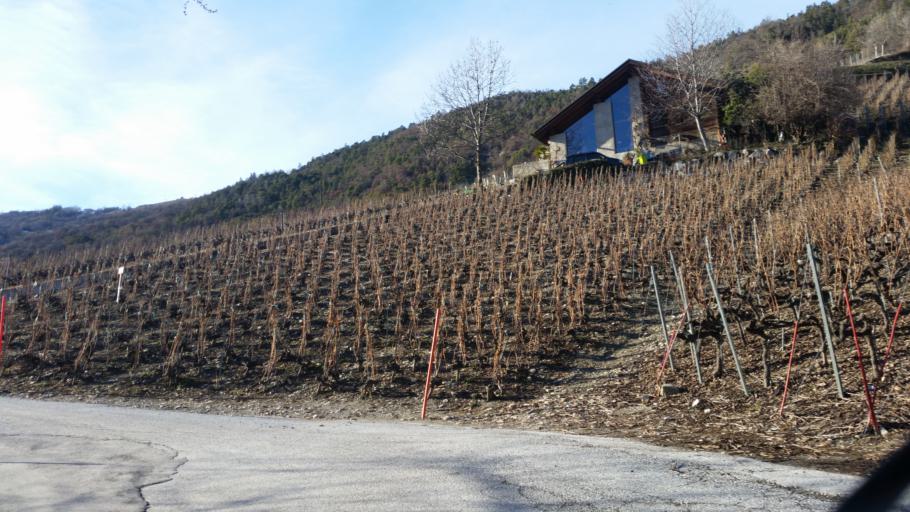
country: CH
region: Valais
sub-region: Sierre District
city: Chermignon-d'en Haut
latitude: 46.2759
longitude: 7.4713
